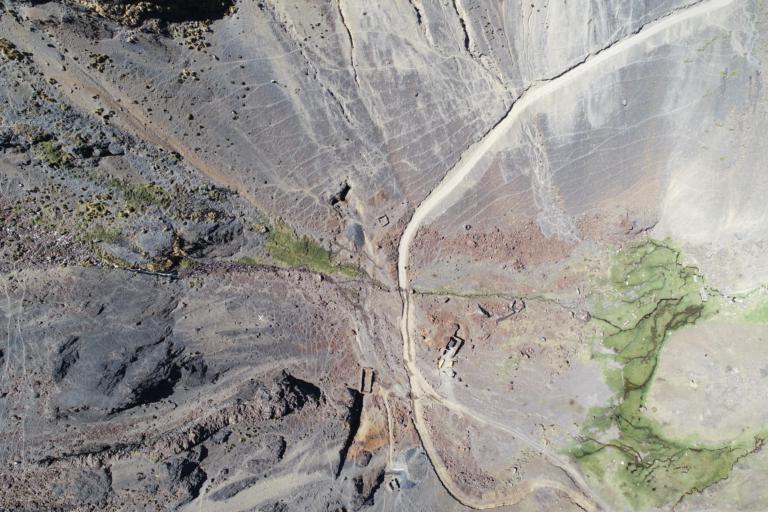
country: BO
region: La Paz
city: La Paz
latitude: -16.6209
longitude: -67.8250
